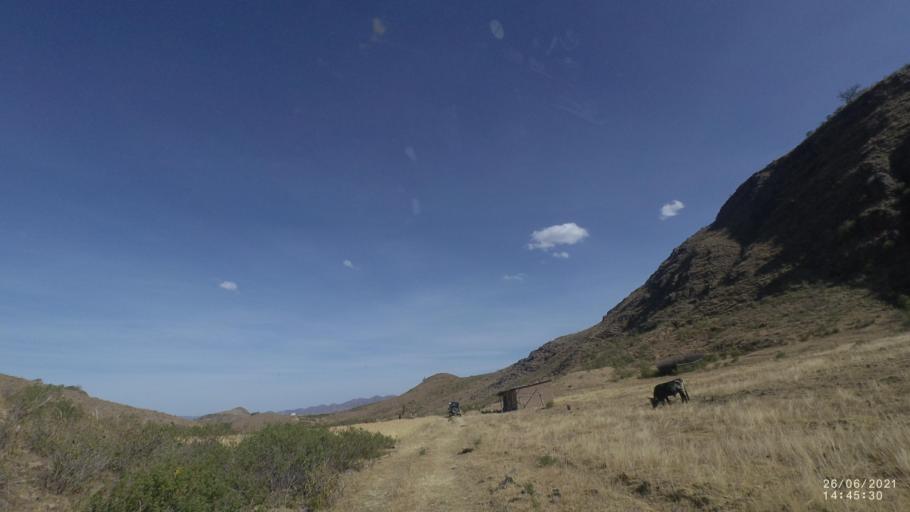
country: BO
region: Cochabamba
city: Mizque
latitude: -17.9146
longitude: -65.6257
